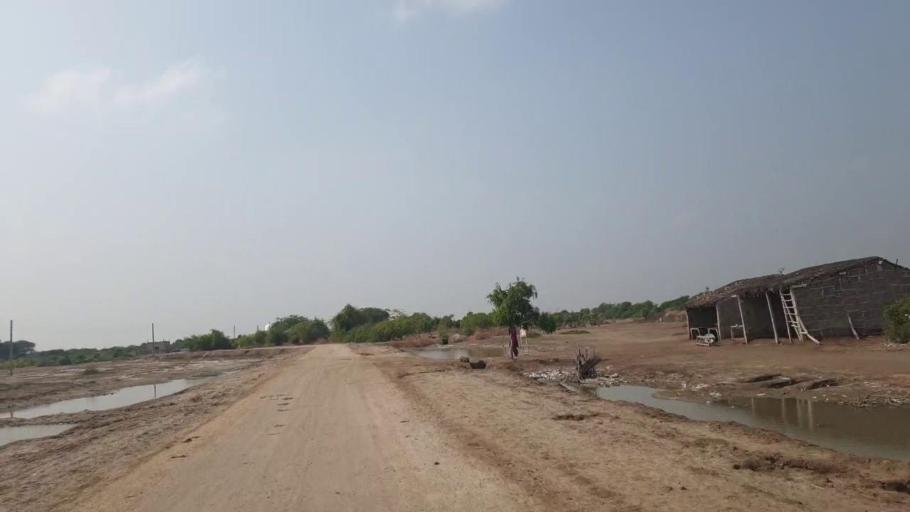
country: PK
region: Sindh
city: Badin
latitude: 24.5458
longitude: 68.6544
